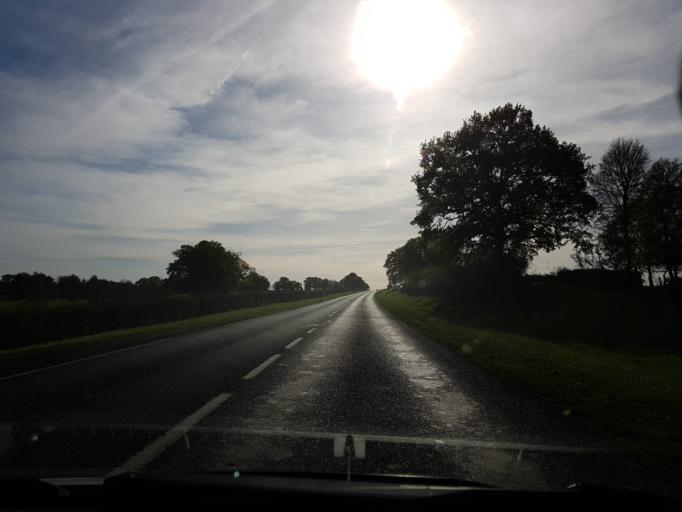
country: FR
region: Bourgogne
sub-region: Departement de l'Yonne
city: Avallon
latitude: 47.4997
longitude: 3.9919
